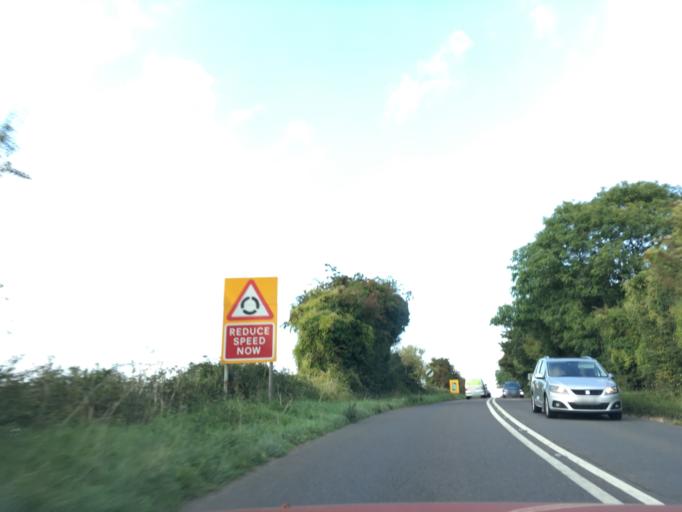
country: GB
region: England
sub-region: Gloucestershire
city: Northleach
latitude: 51.8352
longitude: -1.8397
